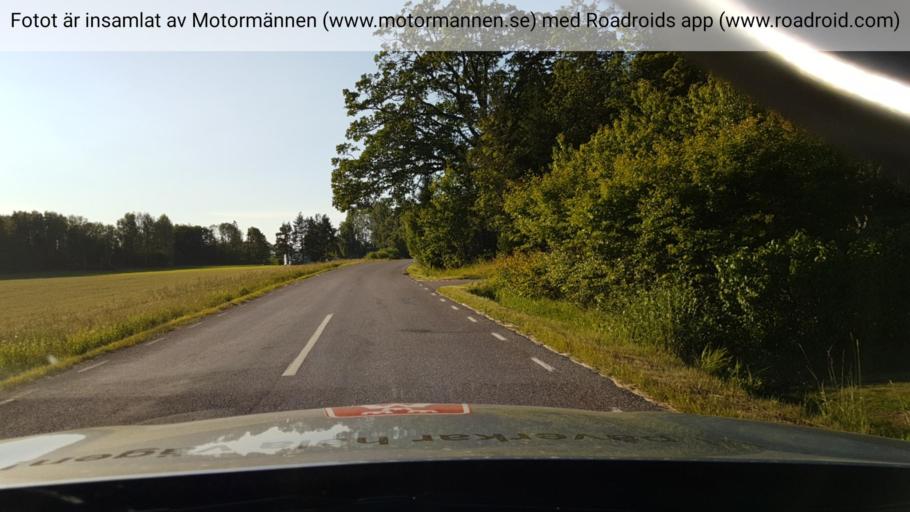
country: SE
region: Vaestmanland
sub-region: Surahammars Kommun
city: Ramnas
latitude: 59.9375
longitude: 16.2946
